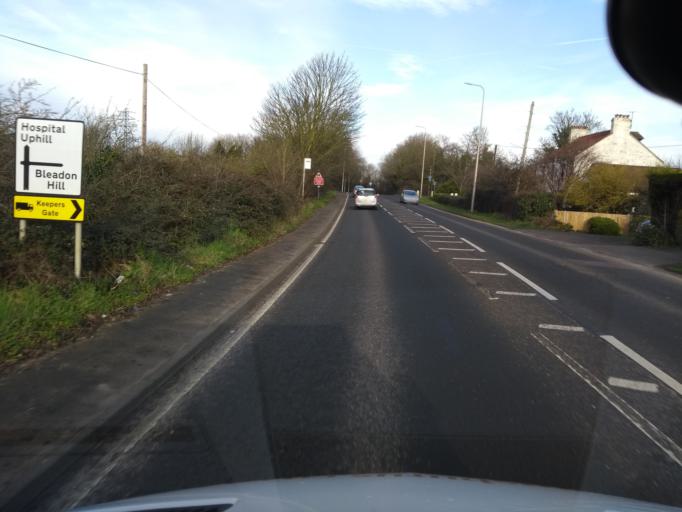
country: GB
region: England
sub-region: North Somerset
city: Bleadon
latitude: 51.3177
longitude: -2.9693
